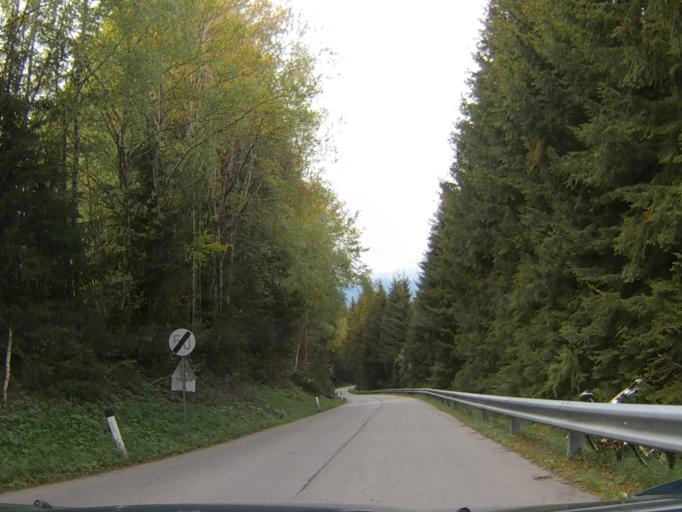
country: AT
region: Carinthia
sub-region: Politischer Bezirk Villach Land
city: Stockenboi
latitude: 46.7346
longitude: 13.5660
